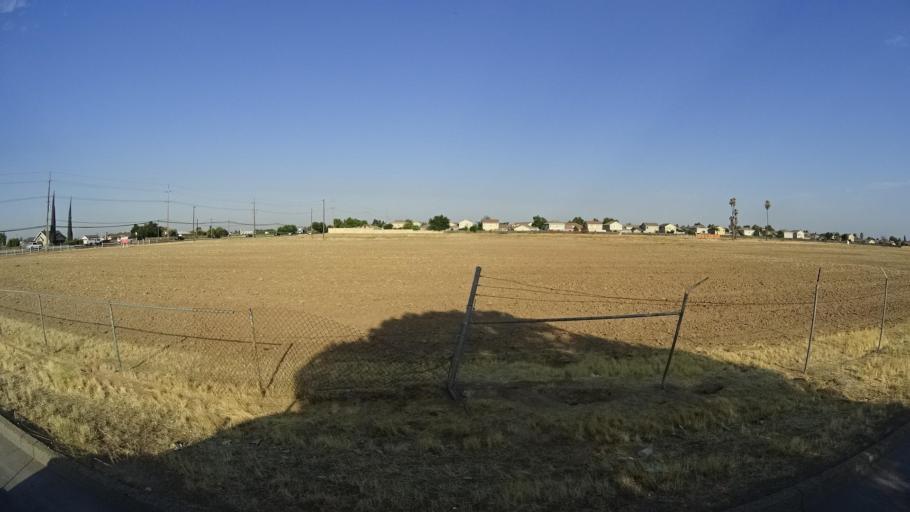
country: US
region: California
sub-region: Fresno County
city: Sunnyside
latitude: 36.7084
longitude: -119.7089
